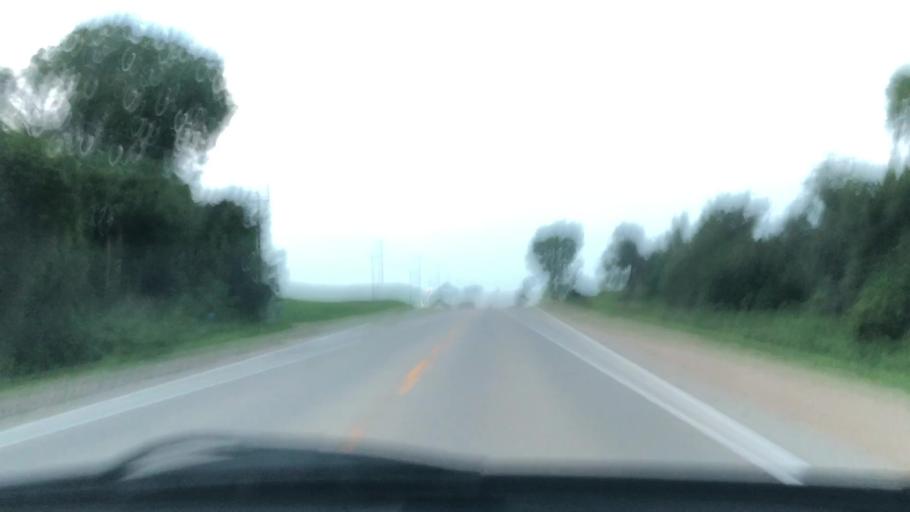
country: US
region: Iowa
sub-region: Linn County
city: Ely
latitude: 41.8508
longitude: -91.6754
